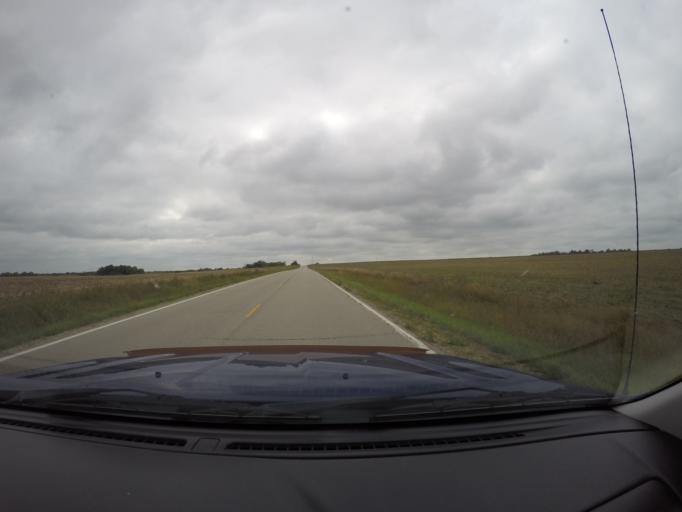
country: US
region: Kansas
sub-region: Morris County
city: Council Grove
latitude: 38.7977
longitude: -96.6635
